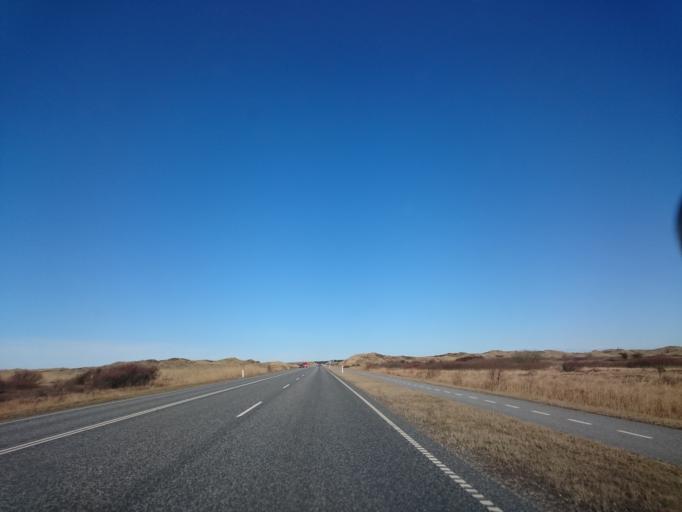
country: DK
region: North Denmark
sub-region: Frederikshavn Kommune
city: Skagen
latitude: 57.6805
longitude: 10.4626
